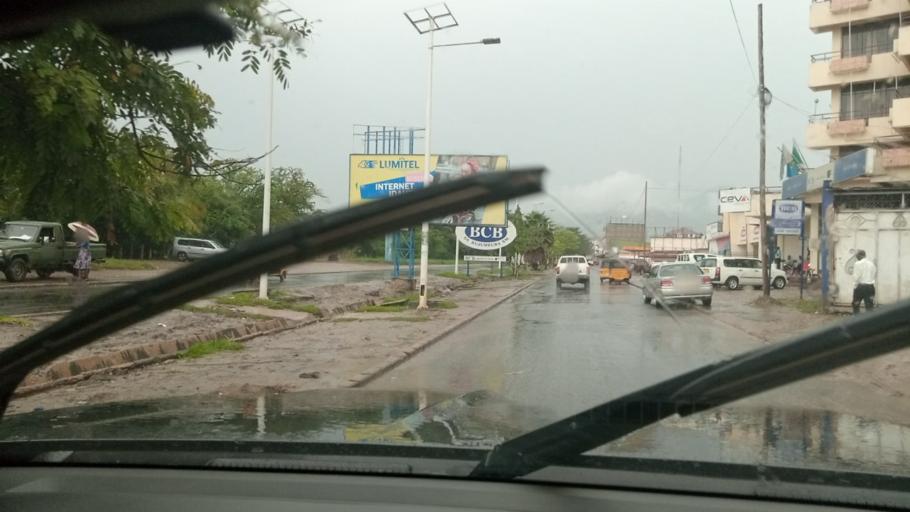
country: BI
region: Bujumbura Mairie
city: Bujumbura
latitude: -3.3791
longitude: 29.3540
